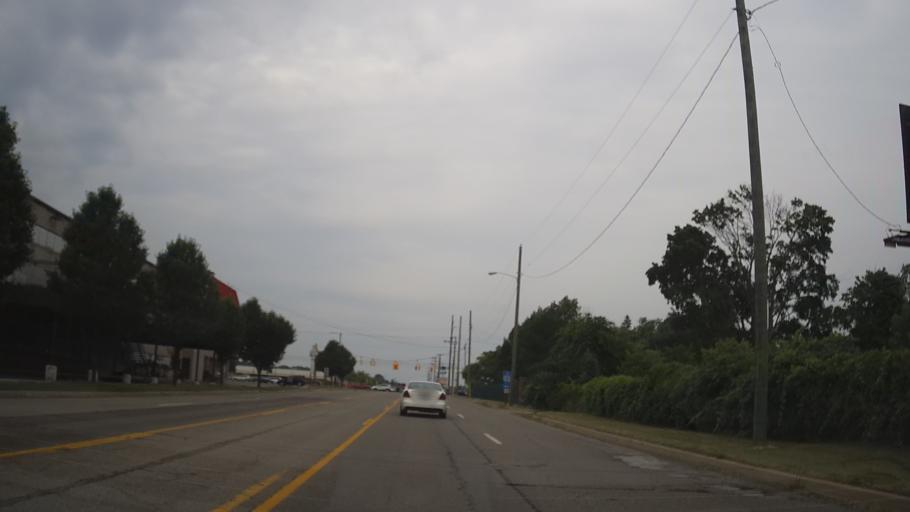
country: US
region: Michigan
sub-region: Macomb County
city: Saint Clair Shores
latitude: 42.5324
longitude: -82.9073
